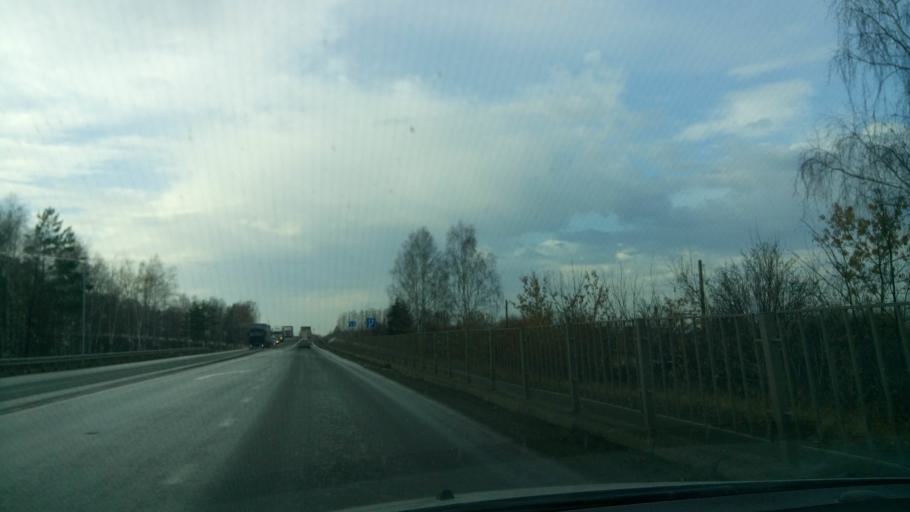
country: RU
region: Sverdlovsk
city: Bogdanovich
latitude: 56.7766
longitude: 62.0067
